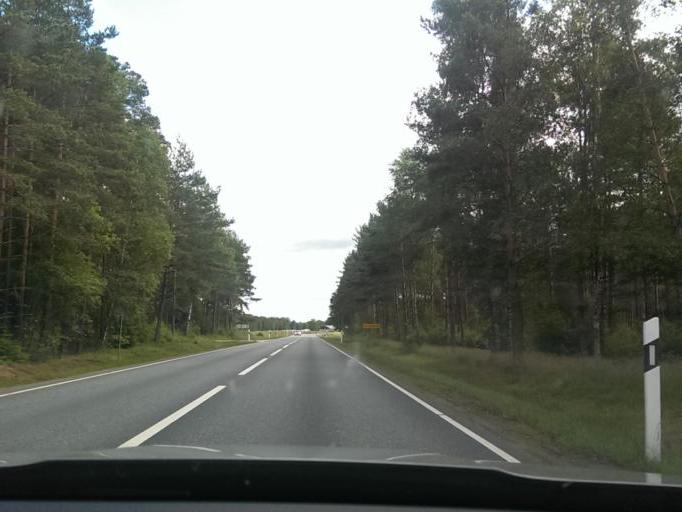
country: SE
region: Joenkoeping
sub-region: Varnamo Kommun
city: Varnamo
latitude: 57.2429
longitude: 13.9978
